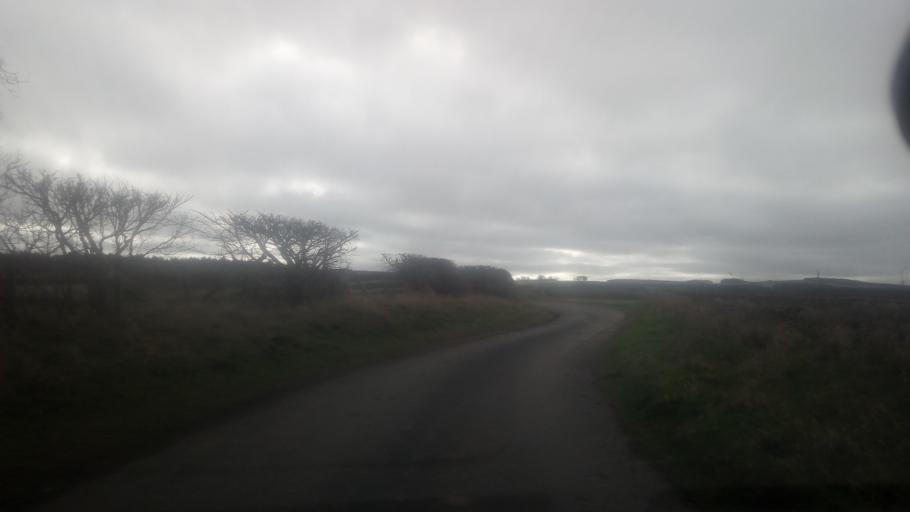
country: GB
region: Scotland
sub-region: The Scottish Borders
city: Kelso
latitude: 55.5672
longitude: -2.5106
